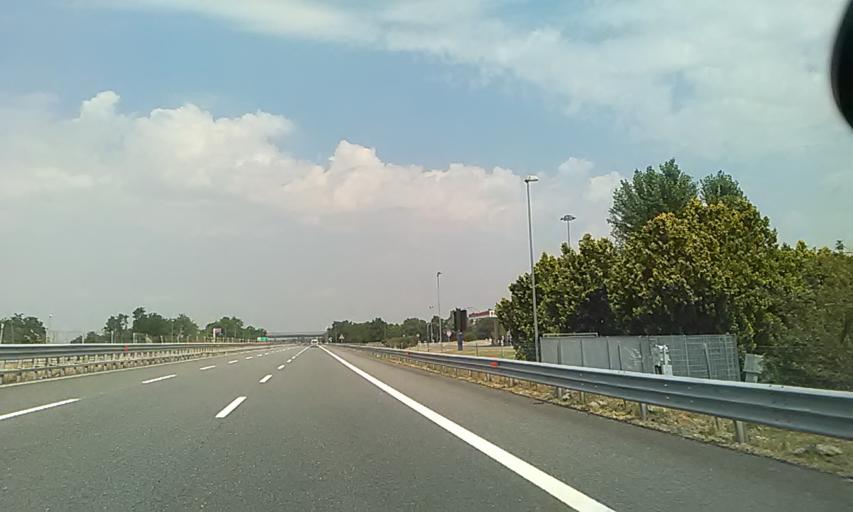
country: IT
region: Piedmont
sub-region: Provincia di Alessandria
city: Castelspina
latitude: 44.8185
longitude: 8.5945
